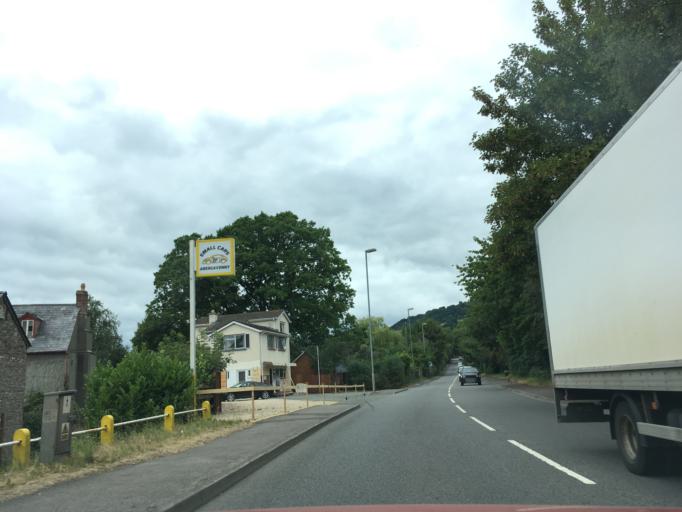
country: GB
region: Wales
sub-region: Monmouthshire
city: Abergavenny
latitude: 51.8269
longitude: -3.0371
